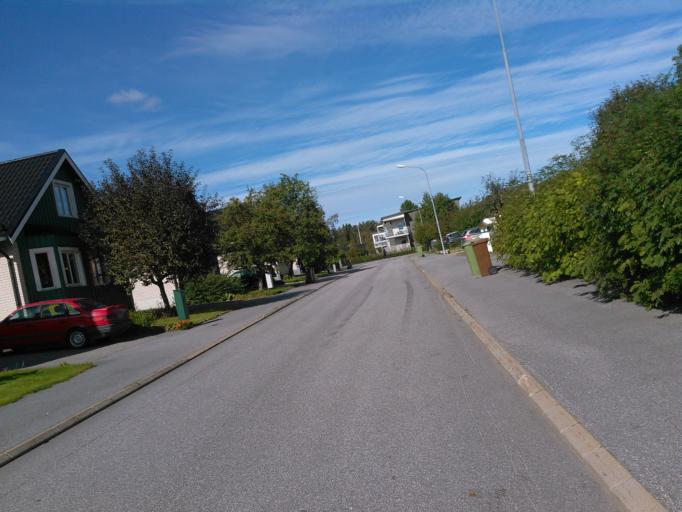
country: SE
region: Vaesterbotten
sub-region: Umea Kommun
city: Umea
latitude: 63.7974
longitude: 20.3128
